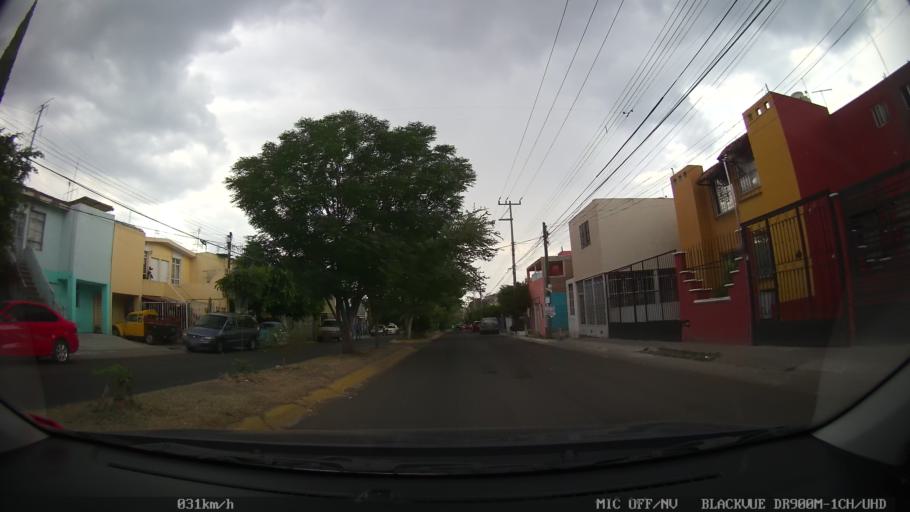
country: MX
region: Jalisco
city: Tlaquepaque
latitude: 20.6262
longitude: -103.2838
